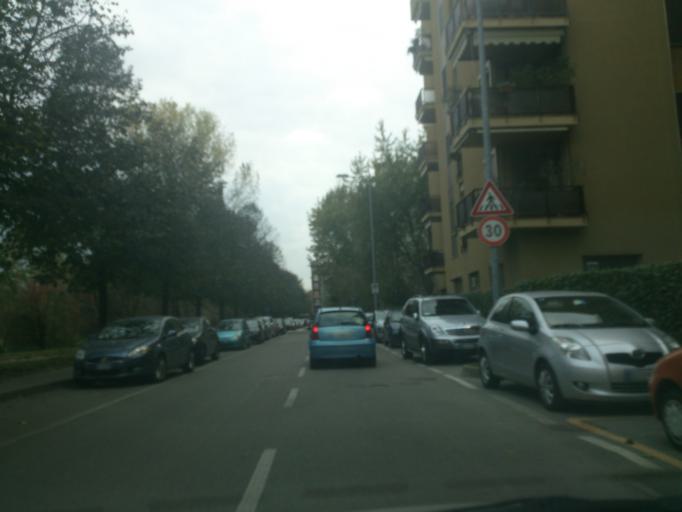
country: IT
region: Lombardy
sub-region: Citta metropolitana di Milano
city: San Donato Milanese
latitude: 45.4147
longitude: 9.2705
